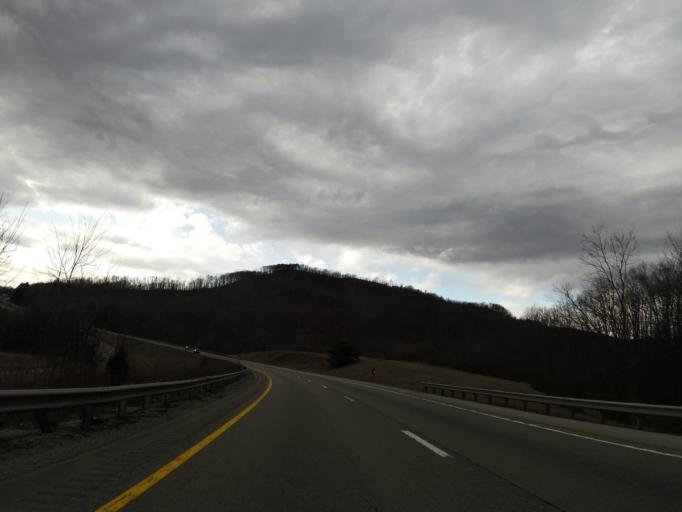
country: US
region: Tennessee
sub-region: Cumberland County
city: Fairfield Glade
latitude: 35.8959
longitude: -84.8422
